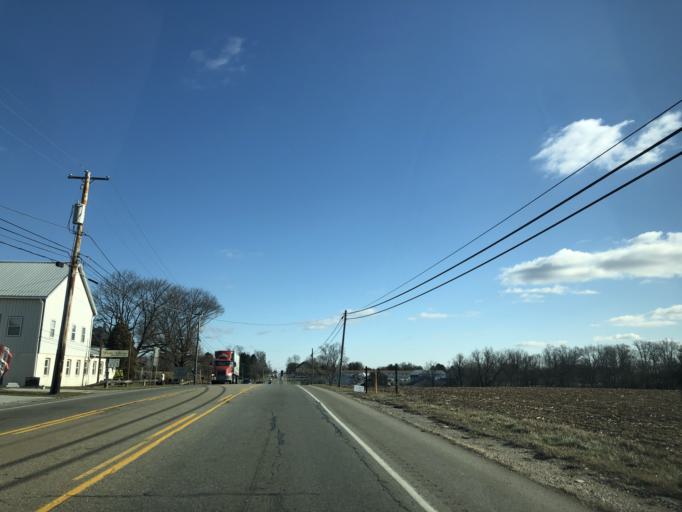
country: US
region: Pennsylvania
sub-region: Chester County
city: Atglen
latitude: 39.9862
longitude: -75.9591
